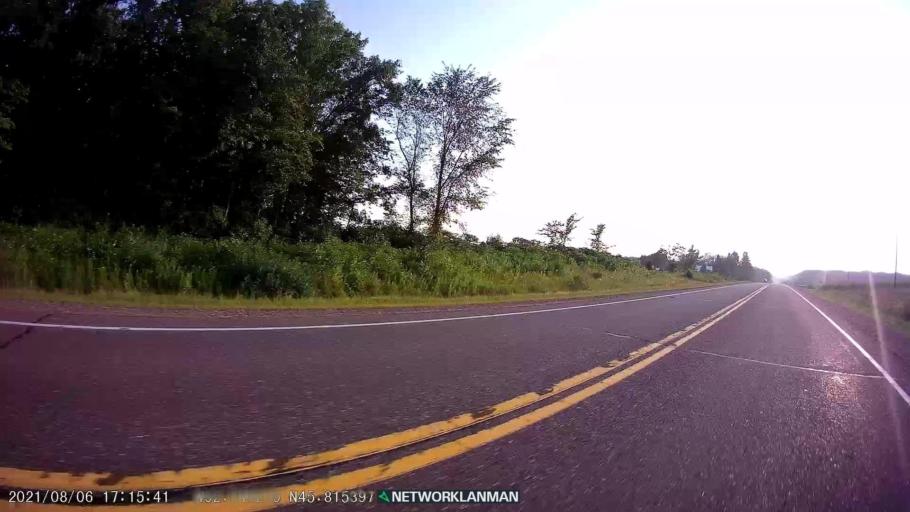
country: US
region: Wisconsin
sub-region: Washburn County
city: Shell Lake
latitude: 45.8156
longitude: -92.0500
